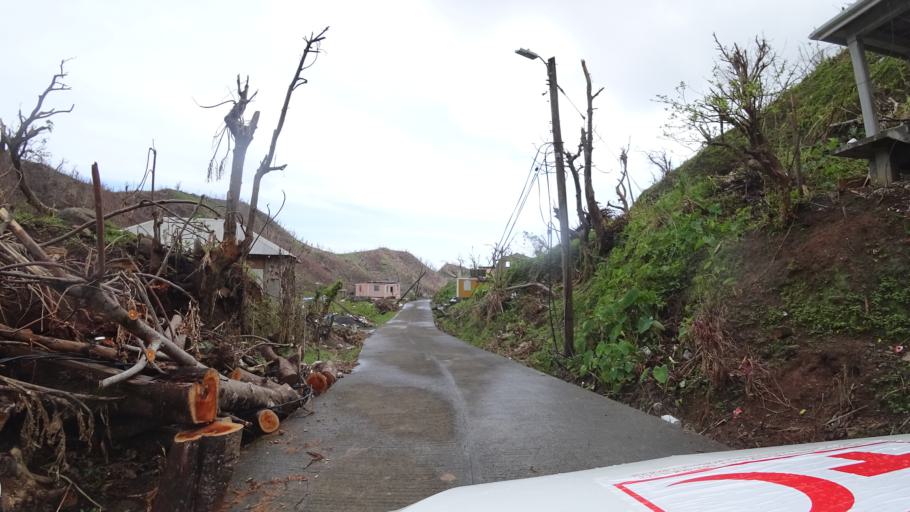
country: DM
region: Saint David
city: Castle Bruce
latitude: 15.4134
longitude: -61.2561
